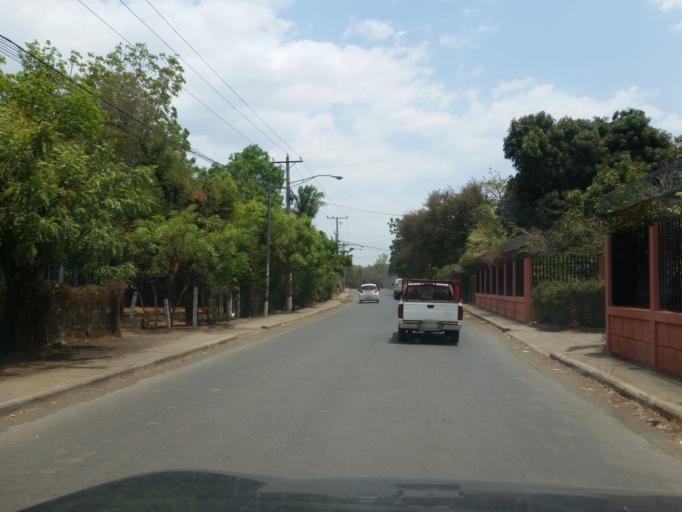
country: NI
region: Managua
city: Managua
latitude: 12.1244
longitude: -86.1704
